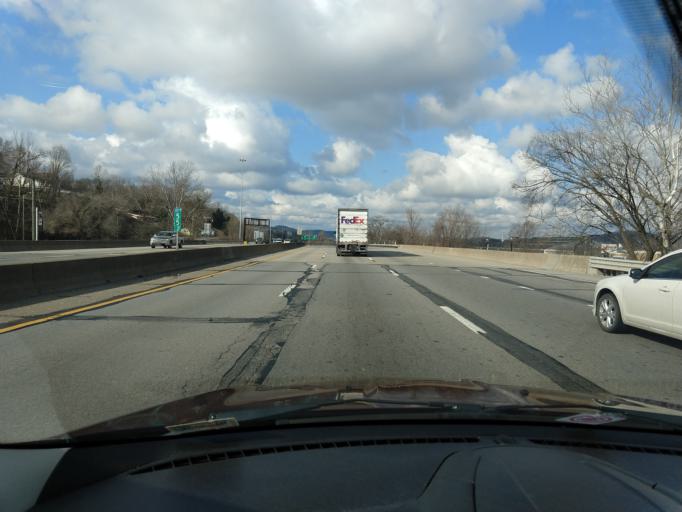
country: US
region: West Virginia
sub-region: Kanawha County
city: South Charleston
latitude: 38.3633
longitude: -81.6907
